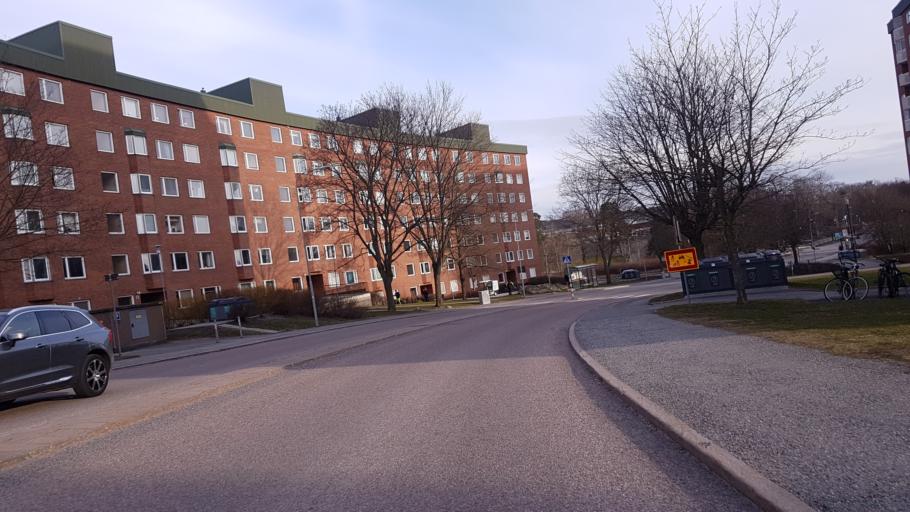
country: SE
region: Stockholm
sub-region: Lidingo
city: Lidingoe
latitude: 59.3480
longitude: 18.1415
